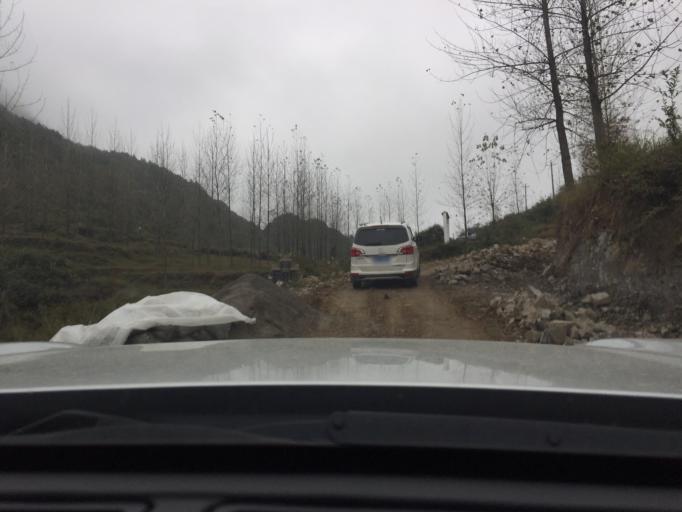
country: CN
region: Guizhou Sheng
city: Jiancha
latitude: 28.1728
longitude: 108.0027
